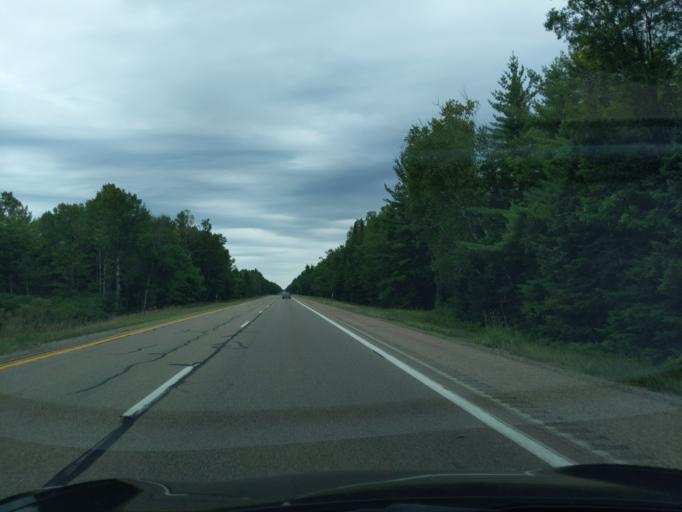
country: US
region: Michigan
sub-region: Roscommon County
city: Houghton Lake
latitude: 44.2209
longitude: -84.7969
